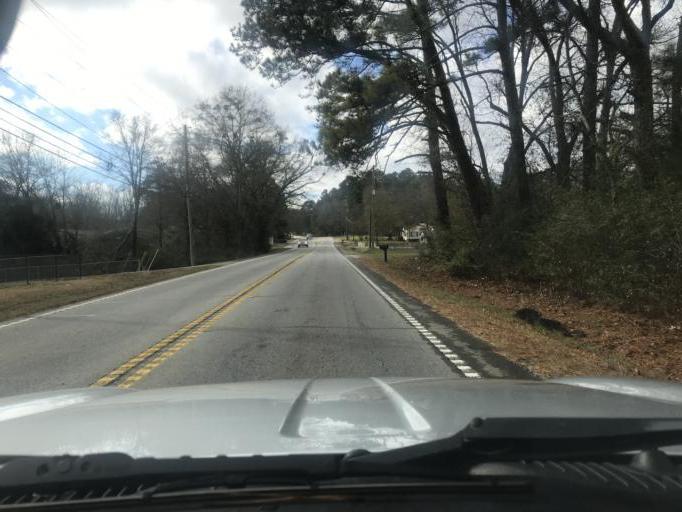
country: US
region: Georgia
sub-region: Barrow County
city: Winder
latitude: 34.0158
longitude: -83.6941
